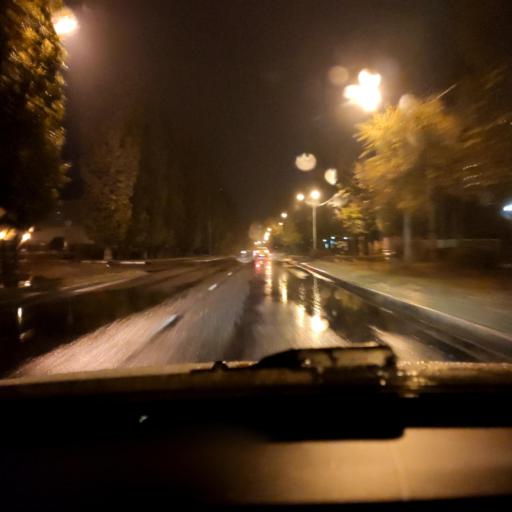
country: RU
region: Voronezj
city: Voronezh
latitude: 51.6919
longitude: 39.2532
